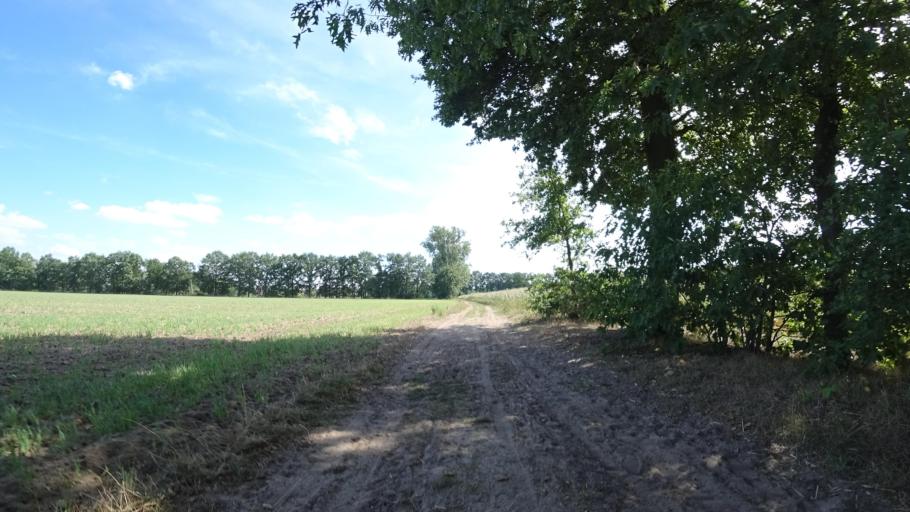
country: DE
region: North Rhine-Westphalia
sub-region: Regierungsbezirk Detmold
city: Guetersloh
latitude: 51.8871
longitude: 8.4138
